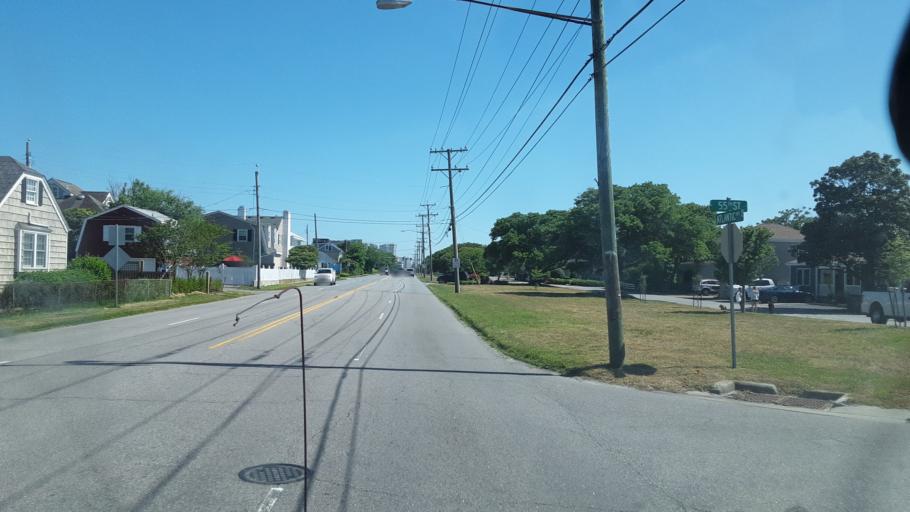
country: US
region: Virginia
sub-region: City of Virginia Beach
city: Virginia Beach
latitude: 36.8818
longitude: -75.9859
